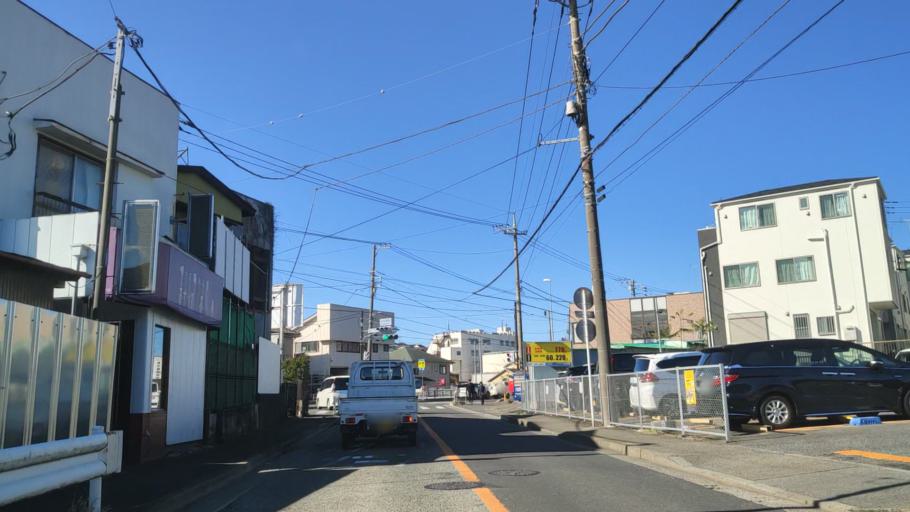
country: JP
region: Kanagawa
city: Minami-rinkan
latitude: 35.4897
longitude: 139.5167
